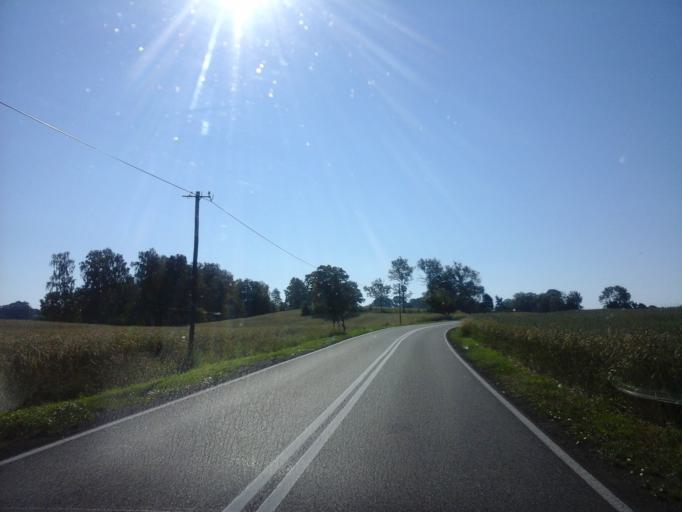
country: PL
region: West Pomeranian Voivodeship
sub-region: Powiat lobeski
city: Wegorzyno
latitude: 53.5057
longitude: 15.6547
